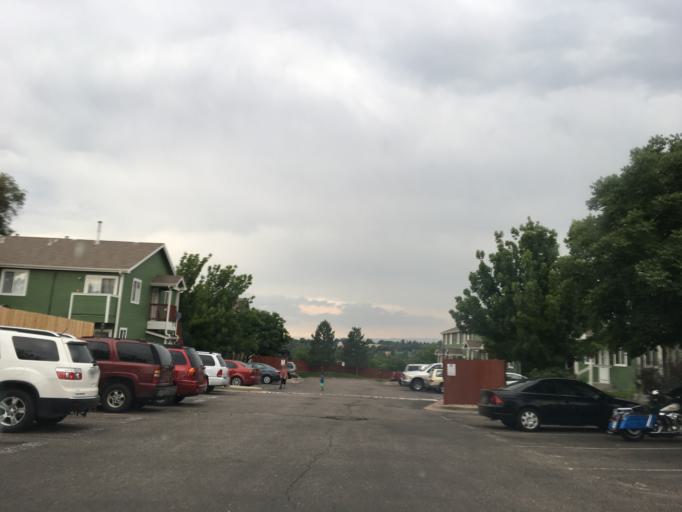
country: US
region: Colorado
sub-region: Arapahoe County
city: Sheridan
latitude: 39.6552
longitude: -105.0284
